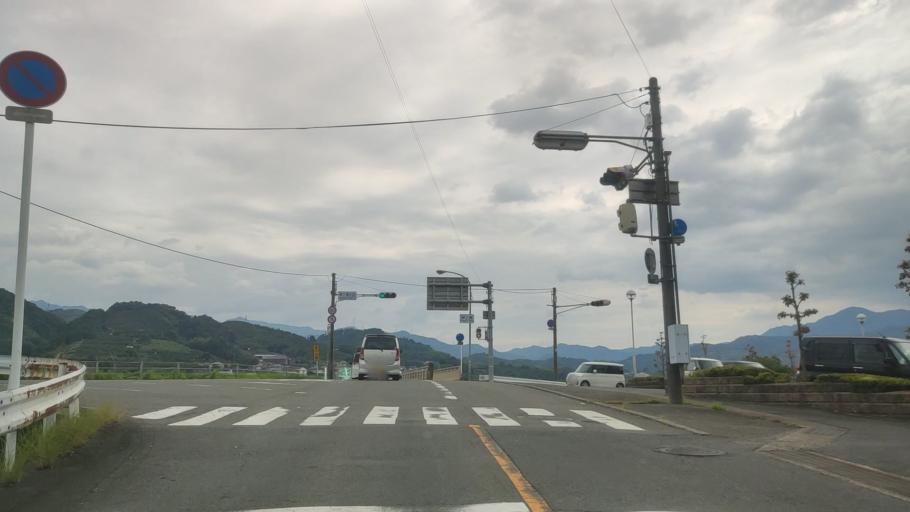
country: JP
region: Wakayama
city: Hashimoto
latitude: 34.3008
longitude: 135.5787
